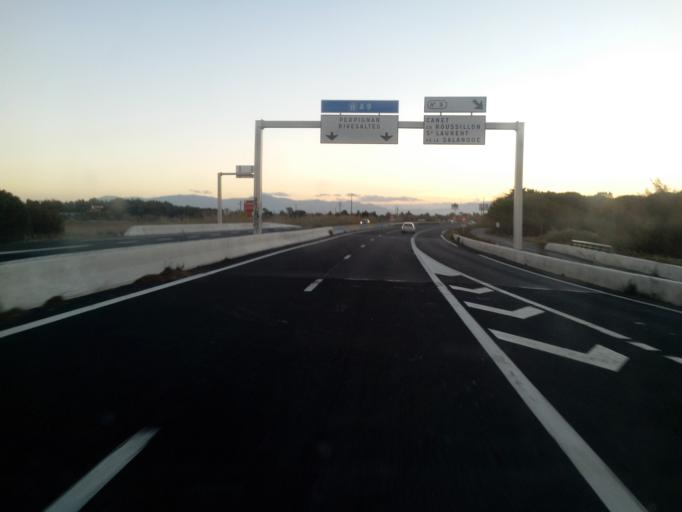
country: FR
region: Languedoc-Roussillon
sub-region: Departement des Pyrenees-Orientales
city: Le Barcares
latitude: 42.7916
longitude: 3.0244
